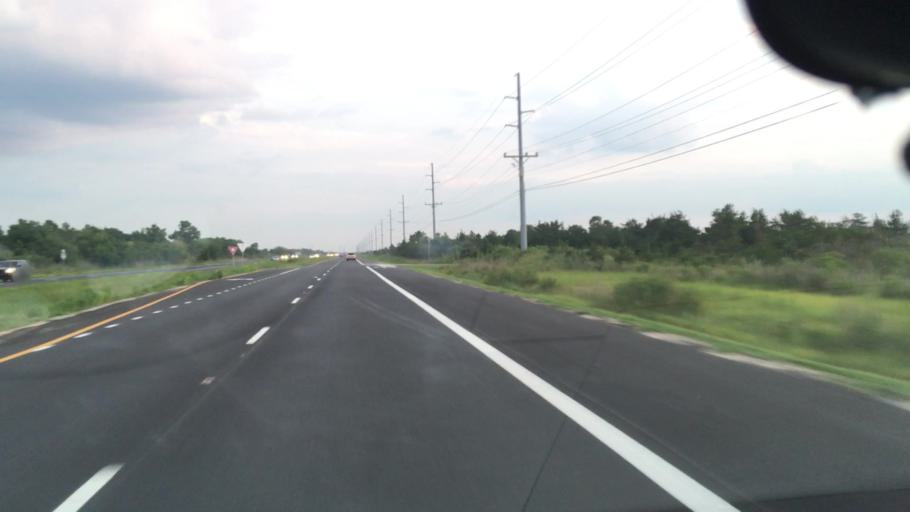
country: US
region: Delaware
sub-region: Sussex County
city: Rehoboth Beach
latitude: 38.6720
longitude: -75.0714
